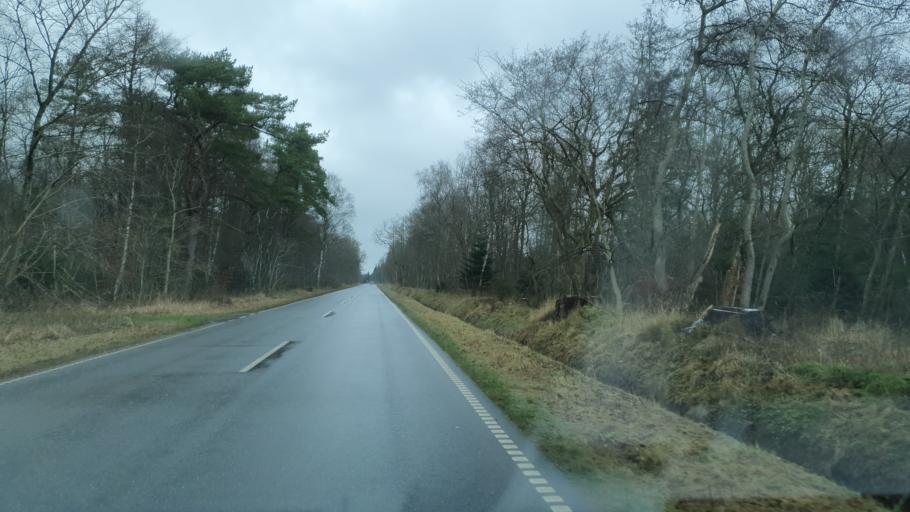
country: DK
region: North Denmark
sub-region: Jammerbugt Kommune
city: Fjerritslev
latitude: 57.1245
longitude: 9.1294
